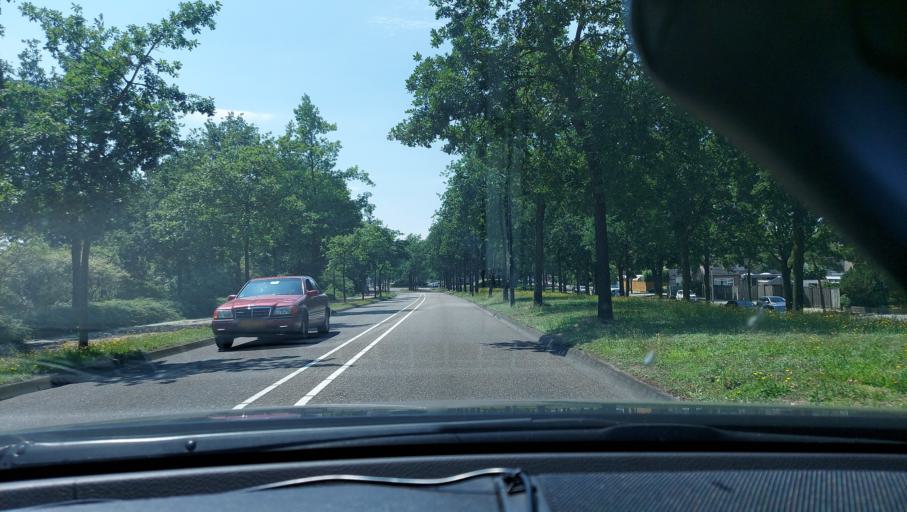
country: NL
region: North Brabant
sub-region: Gemeente Helmond
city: Helmond
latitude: 51.4892
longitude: 5.6800
